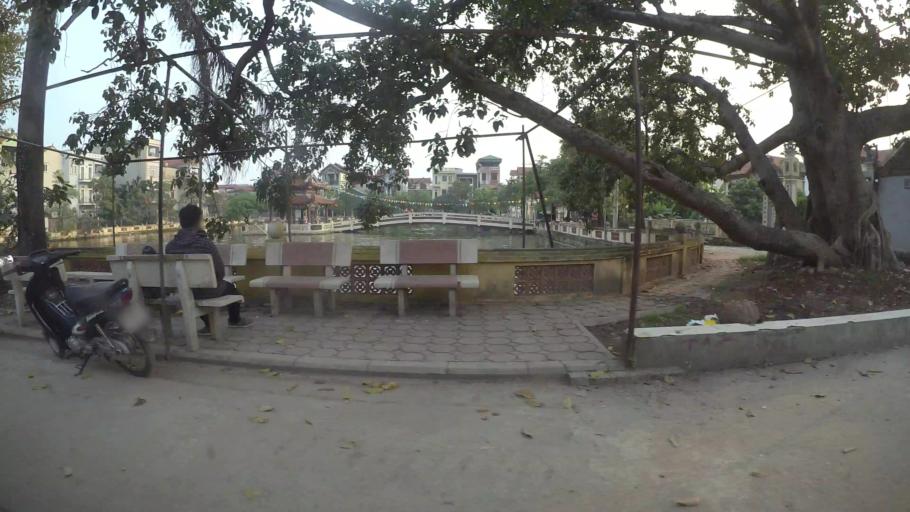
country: VN
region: Ha Noi
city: Cau Dien
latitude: 21.0059
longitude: 105.7240
